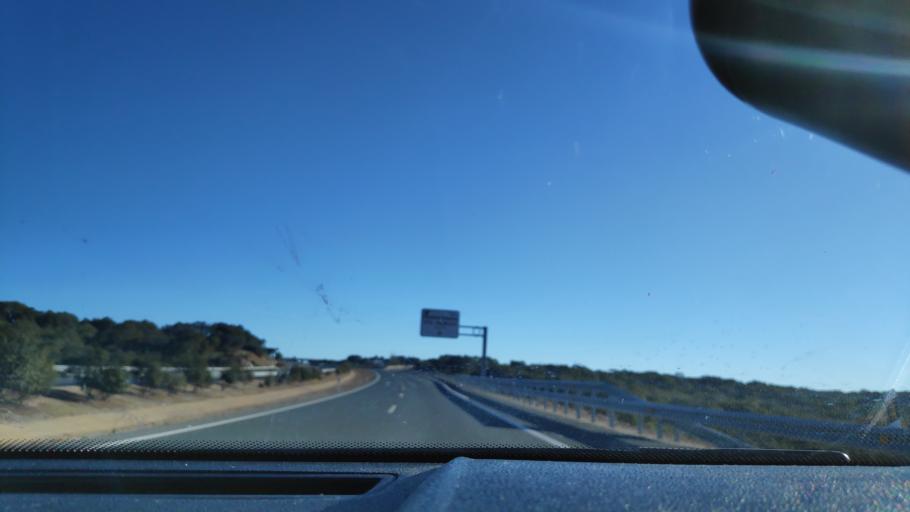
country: ES
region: Andalusia
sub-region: Provincia de Huelva
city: Santa Olalla del Cala
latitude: 37.9231
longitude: -6.2269
